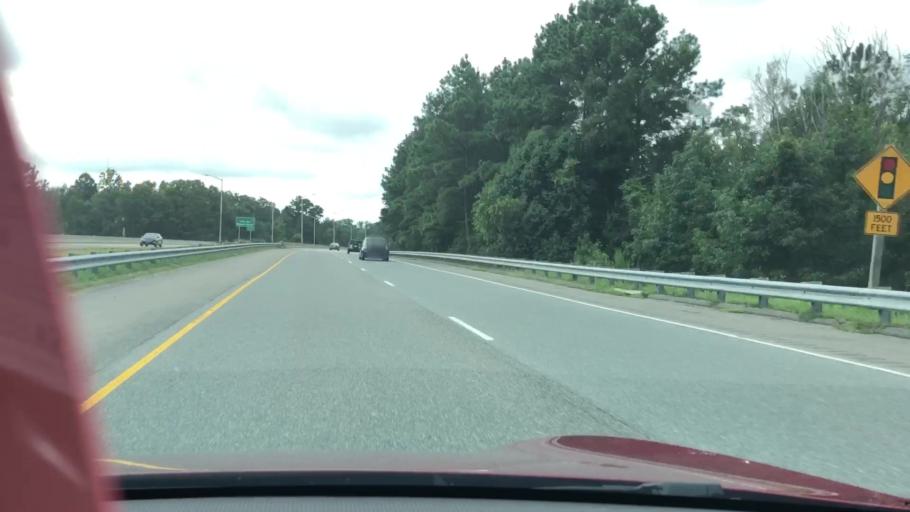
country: US
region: North Carolina
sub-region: Currituck County
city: Moyock
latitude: 36.5680
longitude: -76.1986
